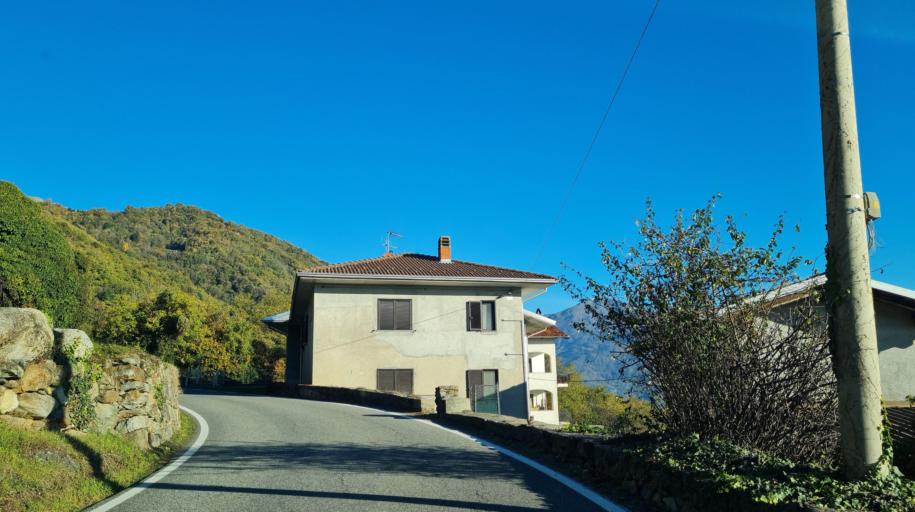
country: IT
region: Piedmont
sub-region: Provincia di Torino
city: Lessolo
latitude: 45.4756
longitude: 7.8055
